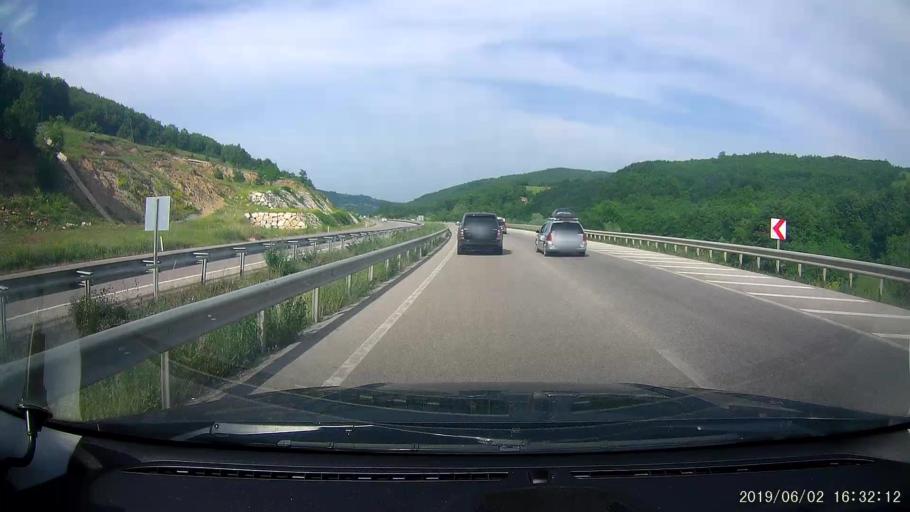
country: TR
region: Samsun
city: Ladik
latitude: 41.0373
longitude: 35.9155
